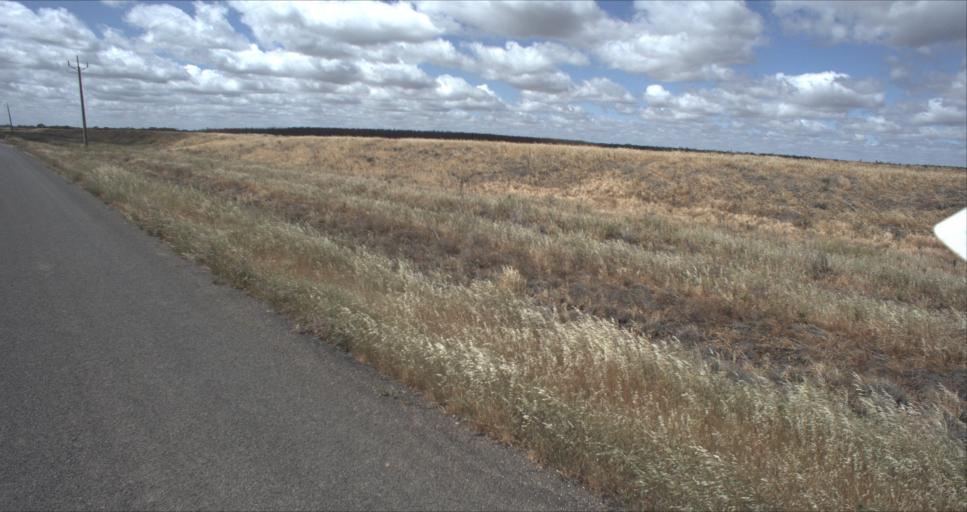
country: AU
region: New South Wales
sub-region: Murrumbidgee Shire
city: Darlington Point
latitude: -34.5781
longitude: 146.1938
